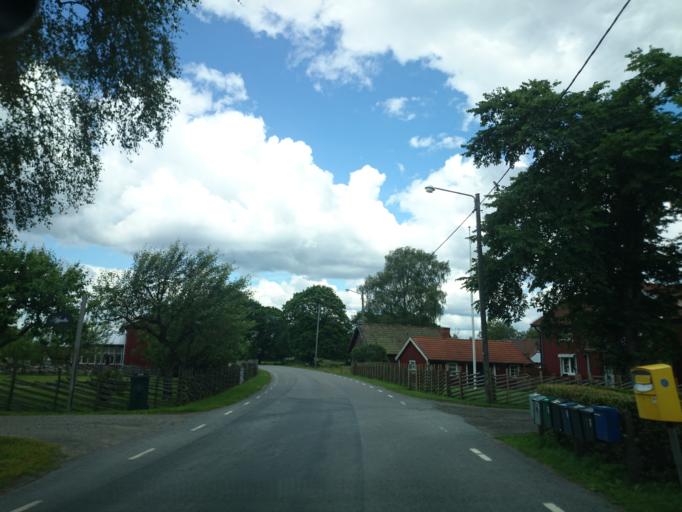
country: SE
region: Joenkoeping
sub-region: Varnamo Kommun
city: Forsheda
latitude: 57.1806
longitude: 13.8452
